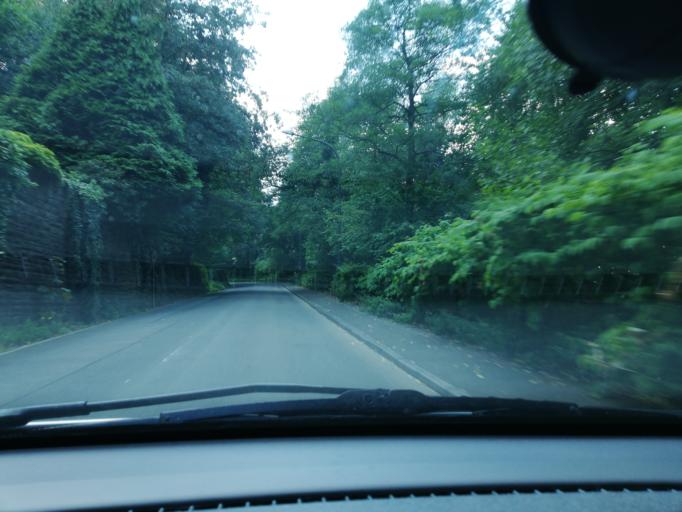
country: DE
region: North Rhine-Westphalia
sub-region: Regierungsbezirk Dusseldorf
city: Wuppertal
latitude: 51.2466
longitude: 7.1150
